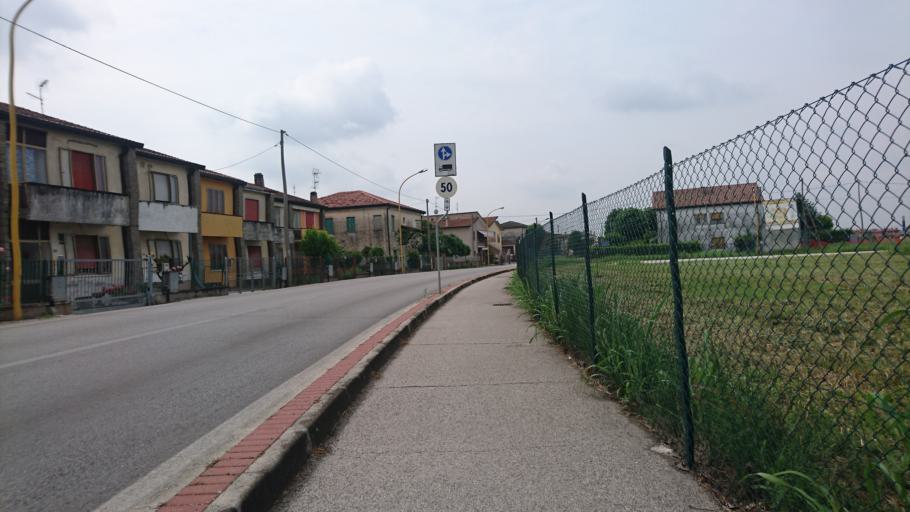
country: IT
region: Veneto
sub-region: Provincia di Padova
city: Villa Estense
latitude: 45.1764
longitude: 11.6707
